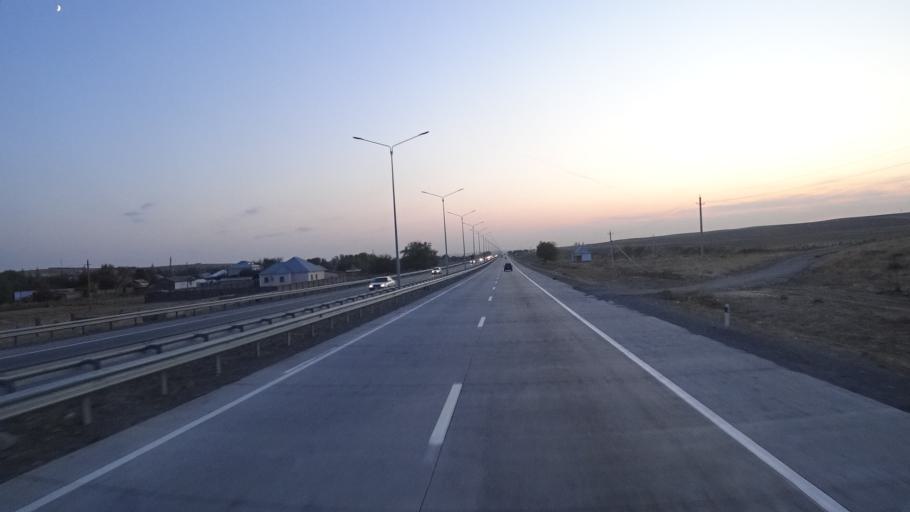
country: KZ
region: Ongtustik Qazaqstan
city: Qazyqurt
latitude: 41.8928
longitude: 69.4495
